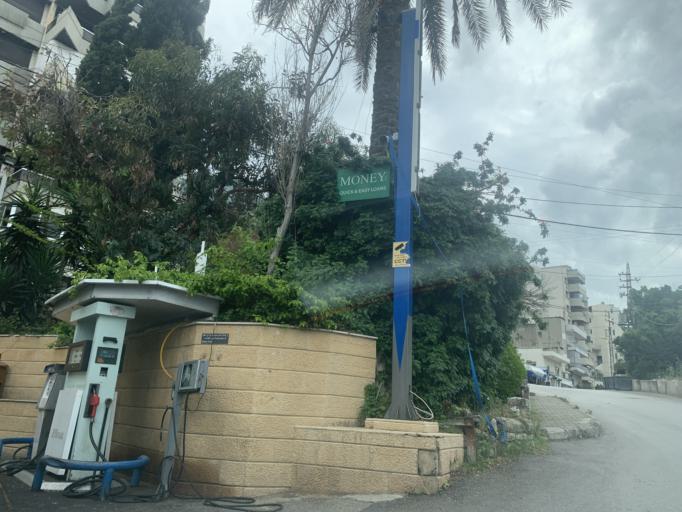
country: LB
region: Mont-Liban
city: Djounie
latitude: 33.9914
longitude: 35.6444
